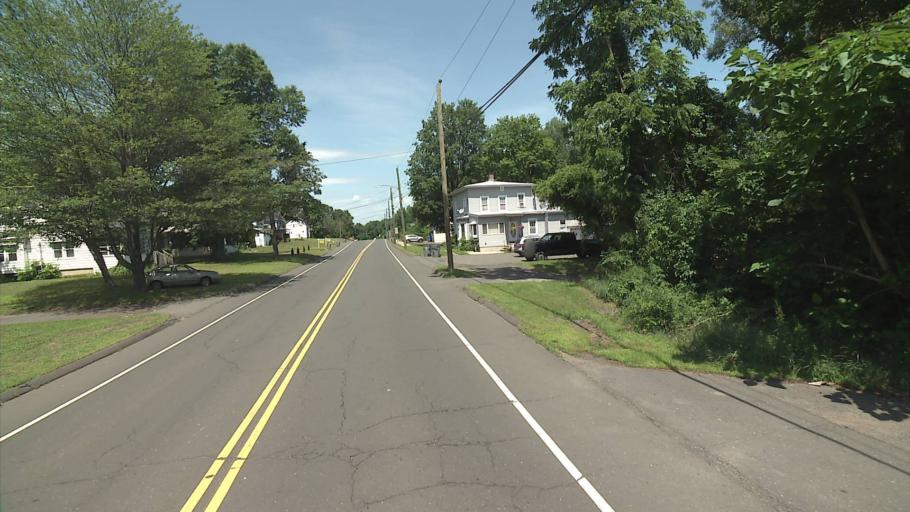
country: US
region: Connecticut
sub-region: Hartford County
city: Plainville
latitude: 41.6708
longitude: -72.8823
